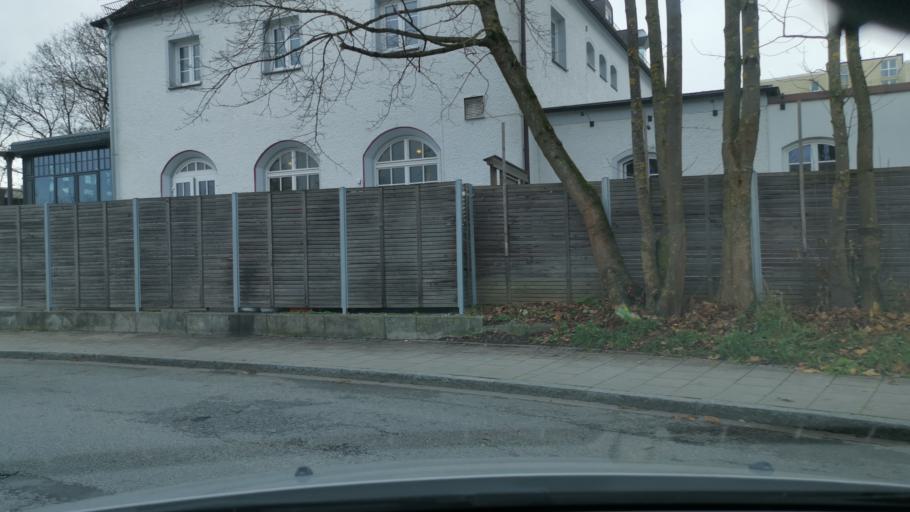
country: DE
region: Bavaria
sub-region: Upper Bavaria
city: Unterschleissheim
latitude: 48.2883
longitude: 11.5817
